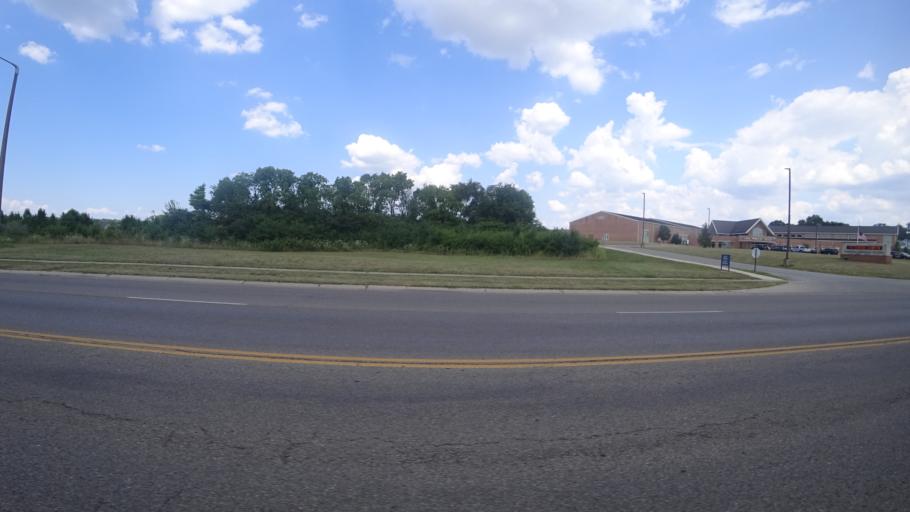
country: US
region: Ohio
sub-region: Butler County
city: New Miami
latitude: 39.4227
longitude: -84.5555
